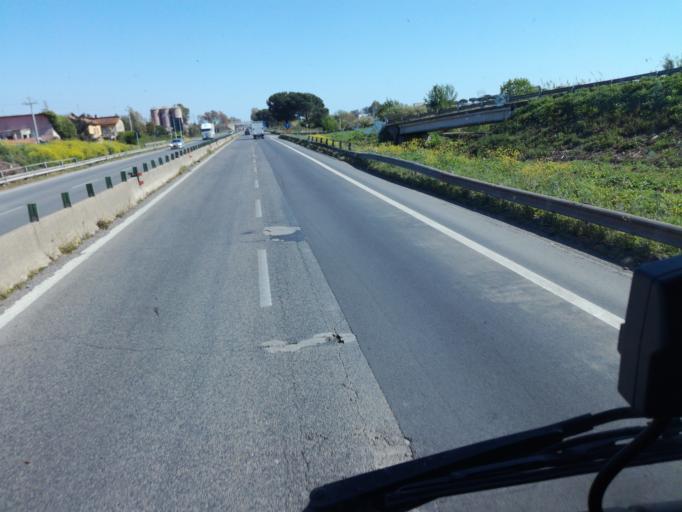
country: IT
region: Latium
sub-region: Provincia di Latina
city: Aprilia
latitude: 41.5723
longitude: 12.6633
